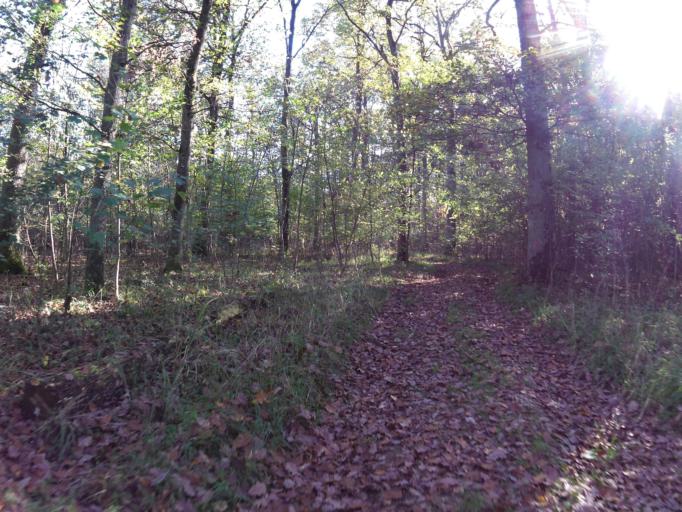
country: DE
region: Bavaria
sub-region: Regierungsbezirk Unterfranken
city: Sulzfeld am Main
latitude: 49.7176
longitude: 10.1013
